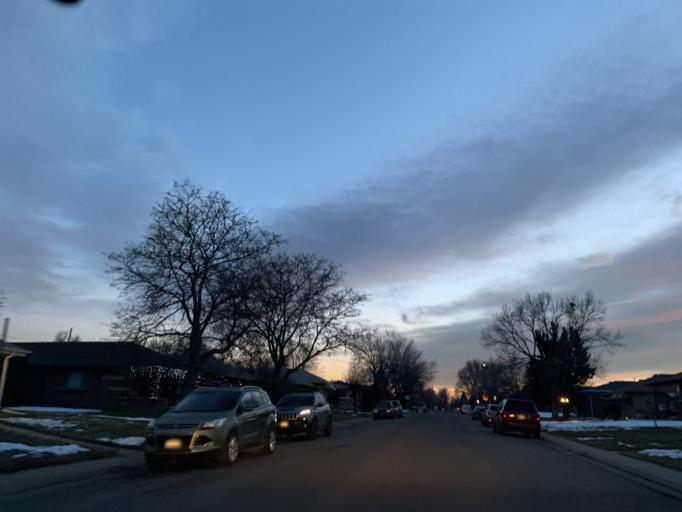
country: US
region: Colorado
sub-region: Adams County
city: Berkley
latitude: 39.7766
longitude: -105.0381
